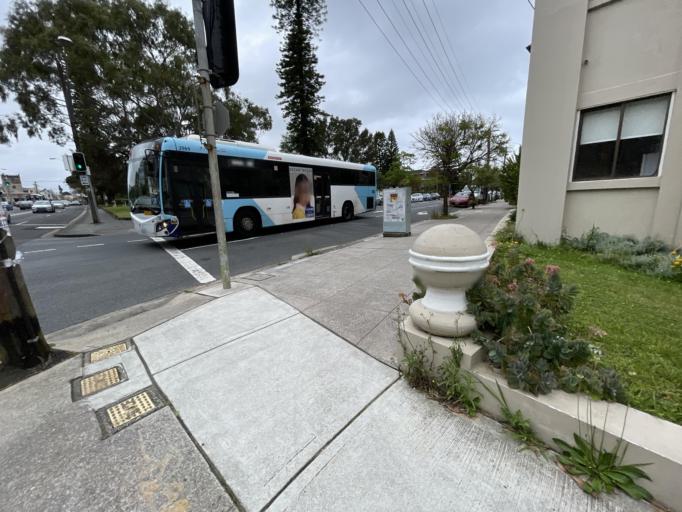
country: AU
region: New South Wales
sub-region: Randwick
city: Randwick
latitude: -33.9183
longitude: 151.2410
